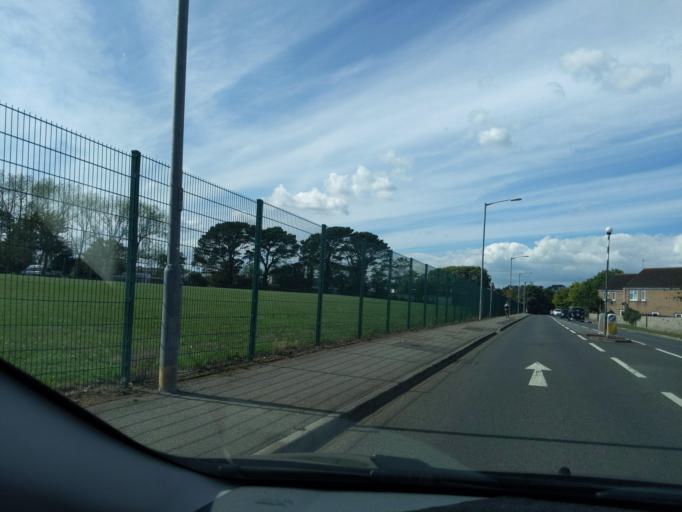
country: GB
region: England
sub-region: Cornwall
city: Torpoint
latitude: 50.3779
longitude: -4.2051
